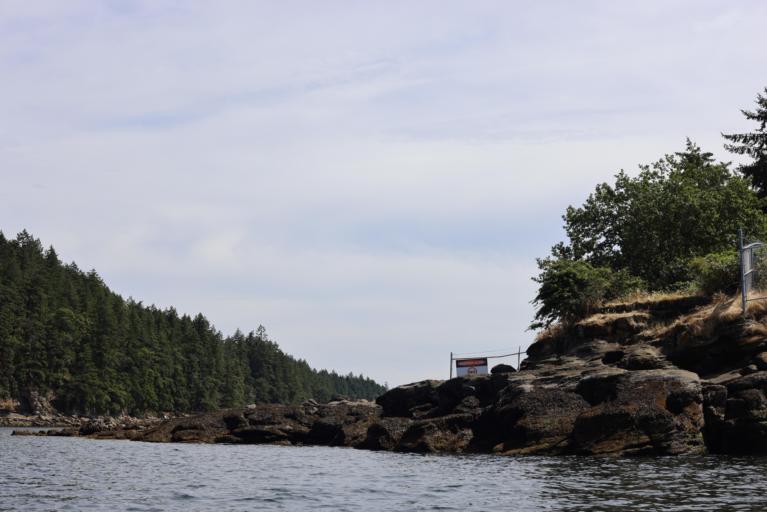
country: CA
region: British Columbia
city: Nanaimo
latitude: 49.1943
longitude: -123.9498
